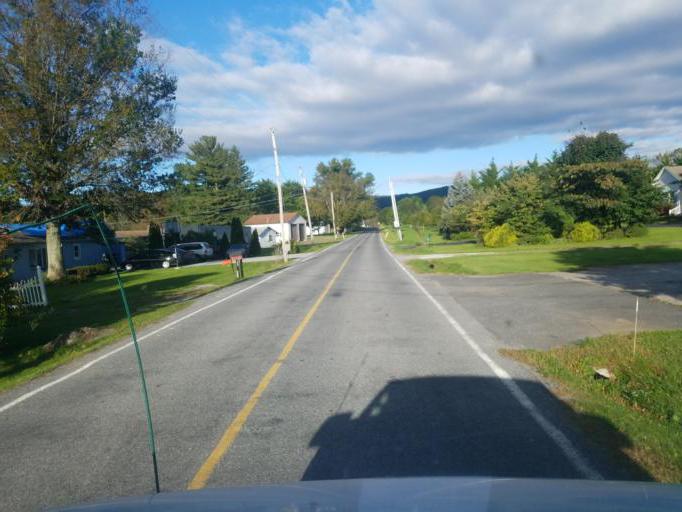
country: US
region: Pennsylvania
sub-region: Adams County
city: Biglerville
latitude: 39.8882
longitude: -77.3438
